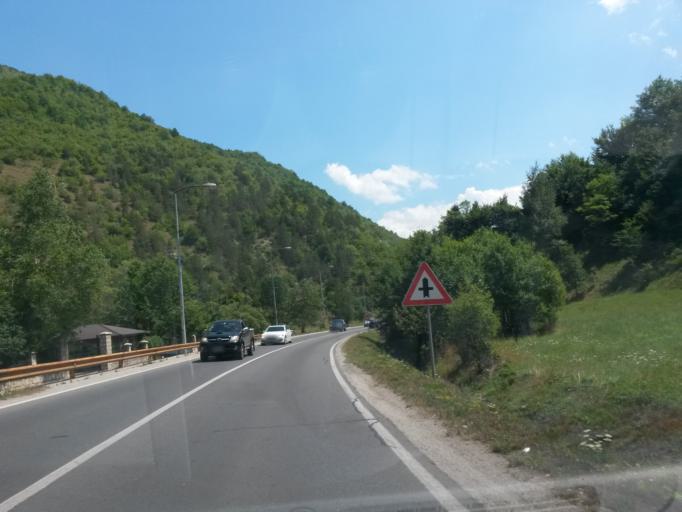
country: BA
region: Federation of Bosnia and Herzegovina
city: Travnik
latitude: 44.2285
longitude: 17.6783
